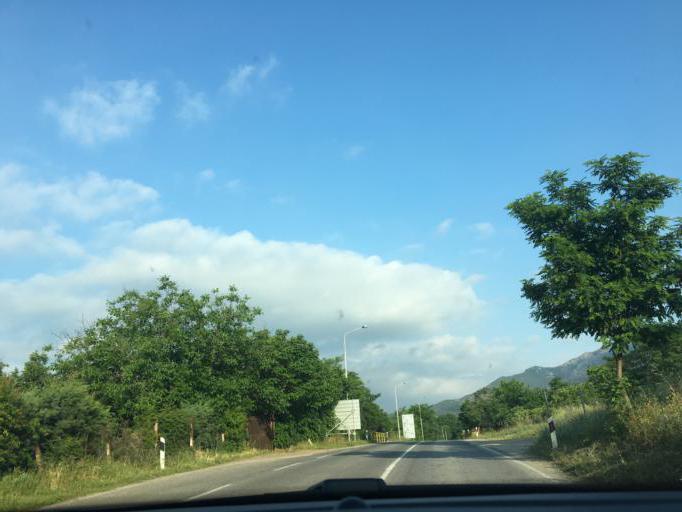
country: MK
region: Valandovo
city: Valandovo
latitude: 41.3170
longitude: 22.5856
